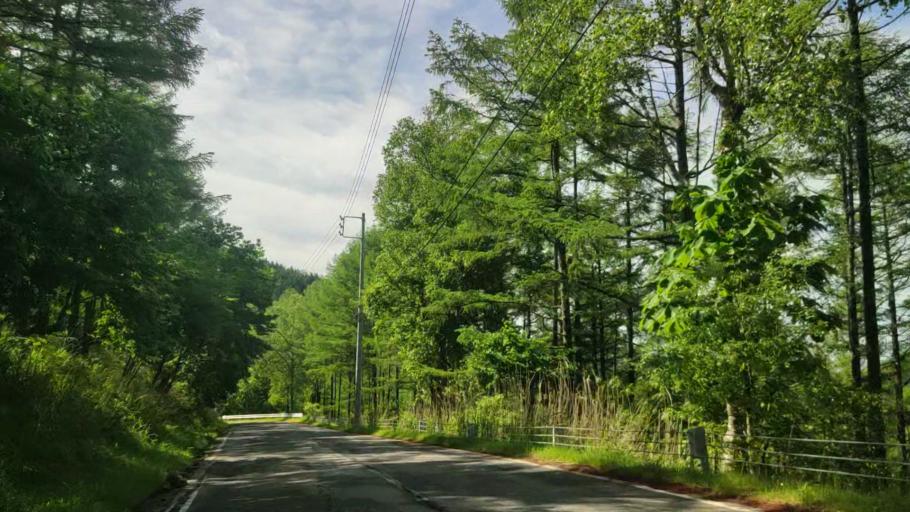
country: JP
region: Nagano
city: Suwa
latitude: 36.0970
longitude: 138.1428
